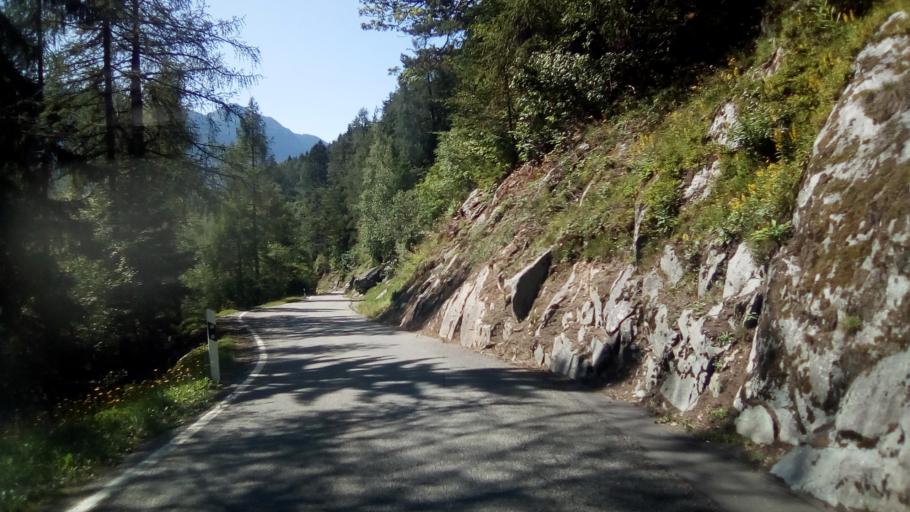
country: CH
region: Valais
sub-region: Saint-Maurice District
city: Salvan
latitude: 46.1310
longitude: 7.0194
